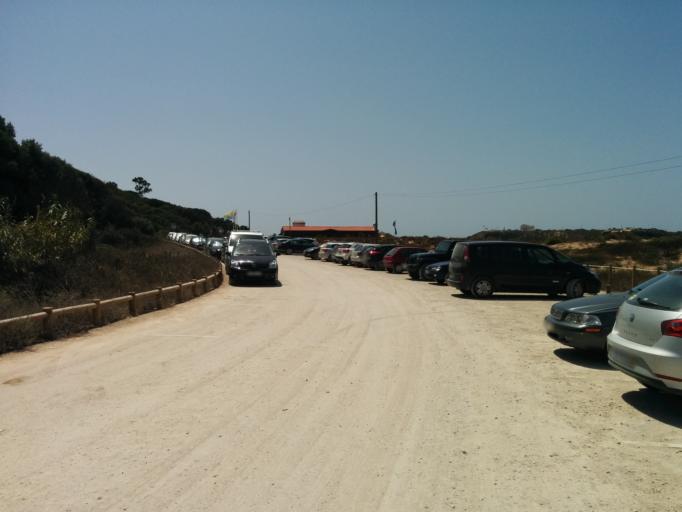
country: PT
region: Beja
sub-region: Odemira
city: Vila Nova de Milfontes
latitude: 37.7195
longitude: -8.7821
